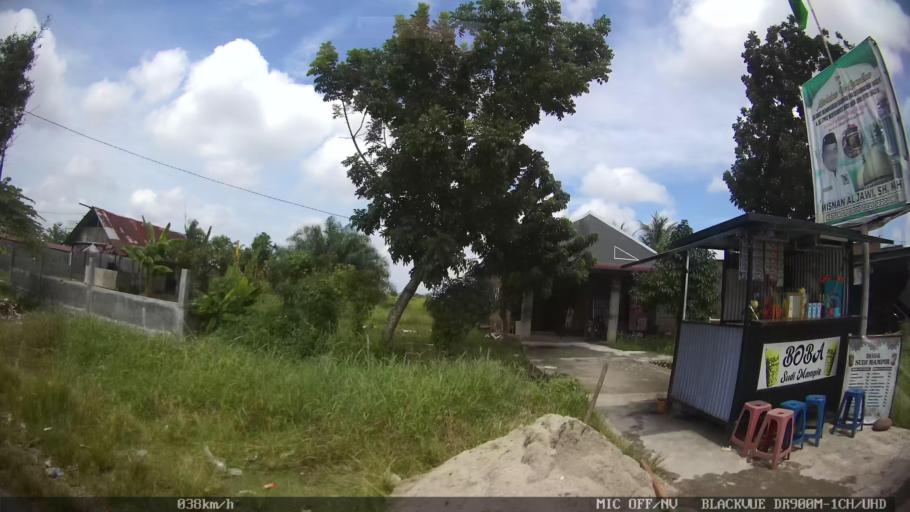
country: ID
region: North Sumatra
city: Percut
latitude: 3.6132
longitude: 98.7815
